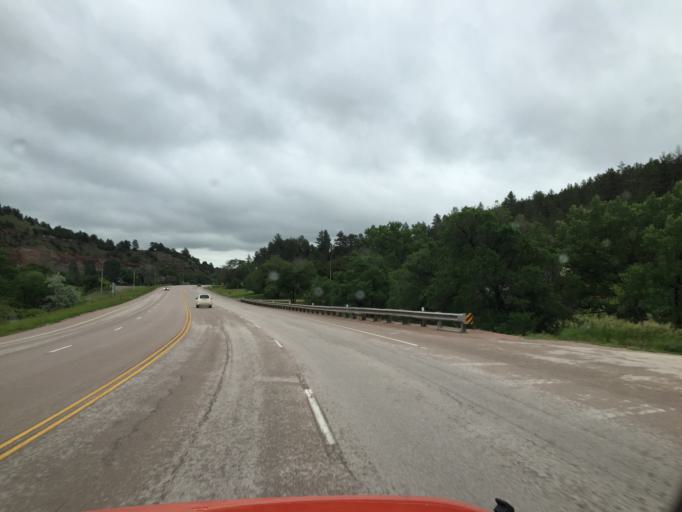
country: US
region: South Dakota
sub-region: Fall River County
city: Hot Springs
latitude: 43.4021
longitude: -103.4337
